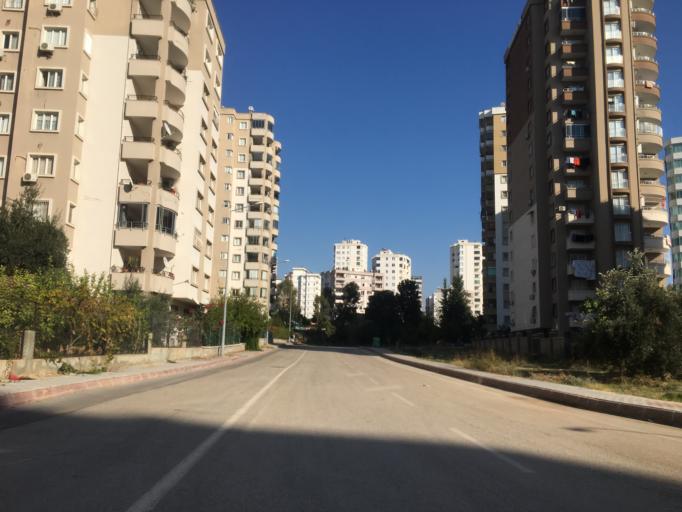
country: TR
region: Adana
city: Seyhan
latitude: 37.0284
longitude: 35.2808
